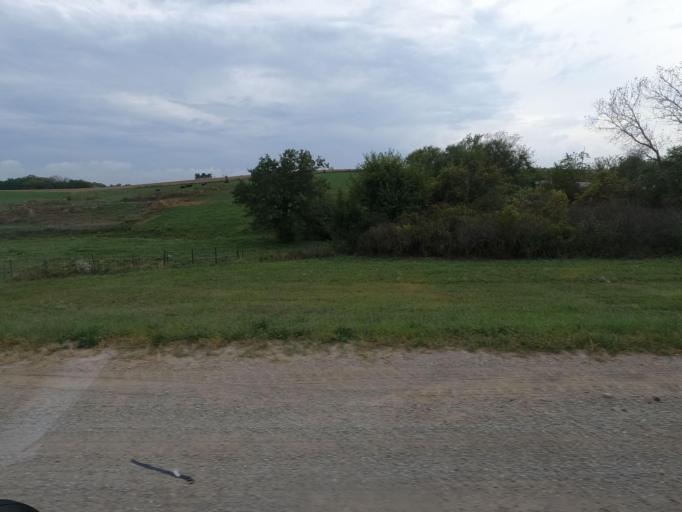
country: US
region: Iowa
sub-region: Van Buren County
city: Keosauqua
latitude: 40.8567
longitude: -92.0825
